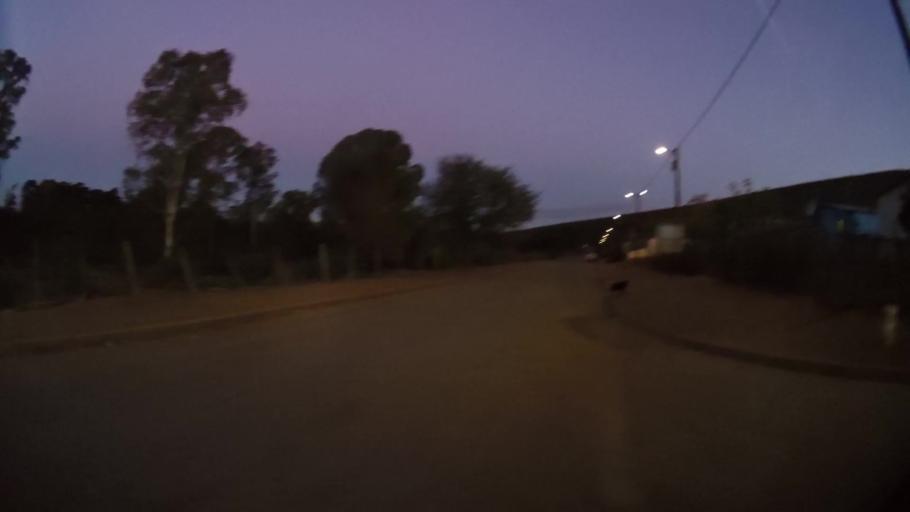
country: ZA
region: Western Cape
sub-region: Eden District Municipality
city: Riversdale
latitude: -34.1063
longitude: 21.2751
